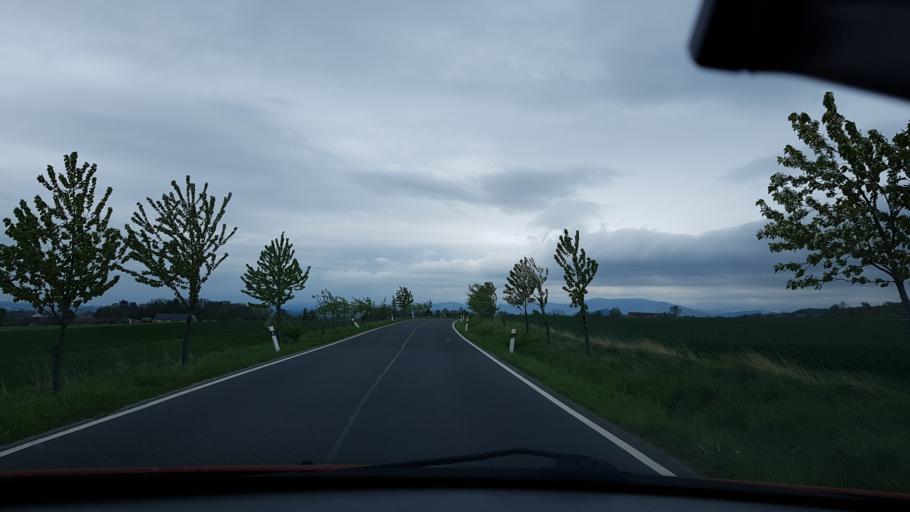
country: CZ
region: Olomoucky
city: Javornik
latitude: 50.4122
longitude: 16.9831
